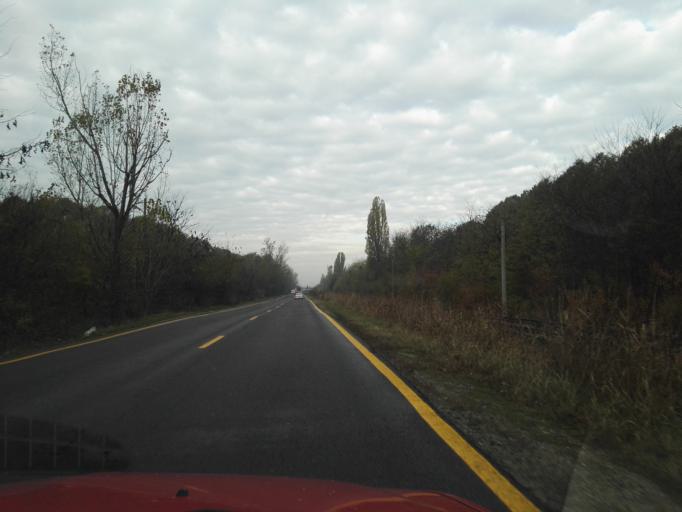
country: RO
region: Ilfov
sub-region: Comuna Magurele
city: Magurele
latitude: 44.3551
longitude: 26.0493
